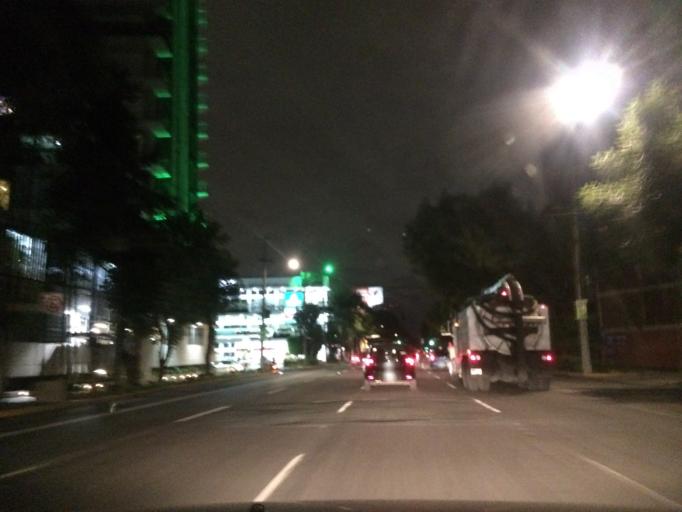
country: MX
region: Mexico City
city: Coyoacan
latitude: 19.3646
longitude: -99.1625
